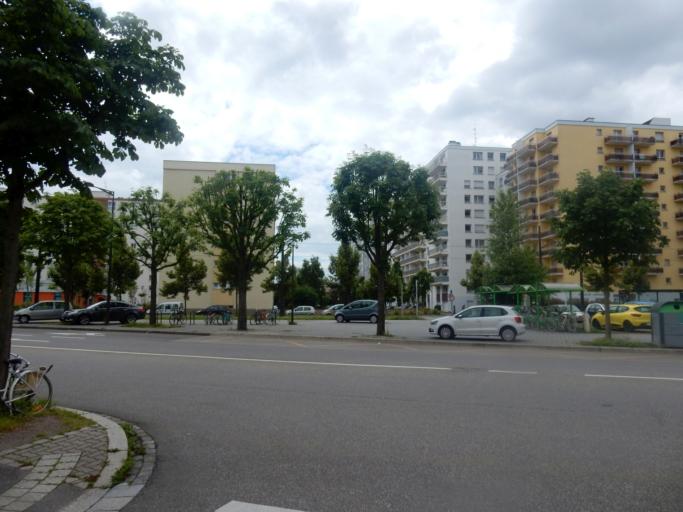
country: FR
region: Alsace
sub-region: Departement du Bas-Rhin
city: Strasbourg
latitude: 48.5806
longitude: 7.7768
